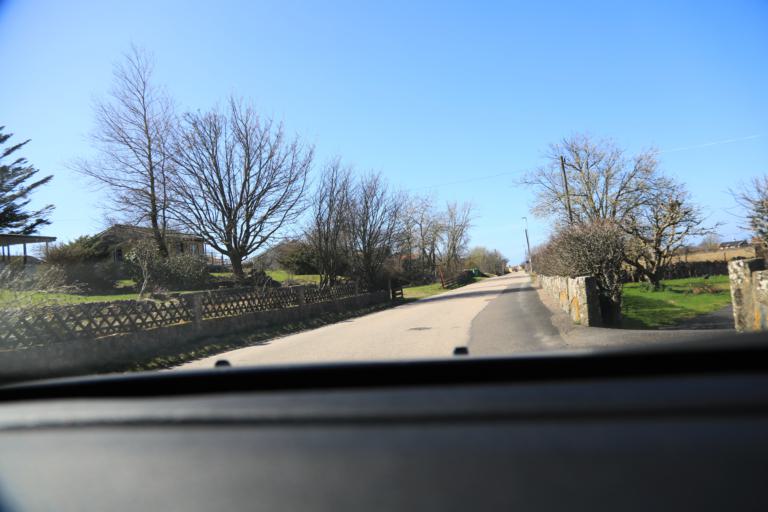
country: SE
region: Halland
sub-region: Varbergs Kommun
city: Varberg
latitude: 57.1189
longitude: 12.2098
